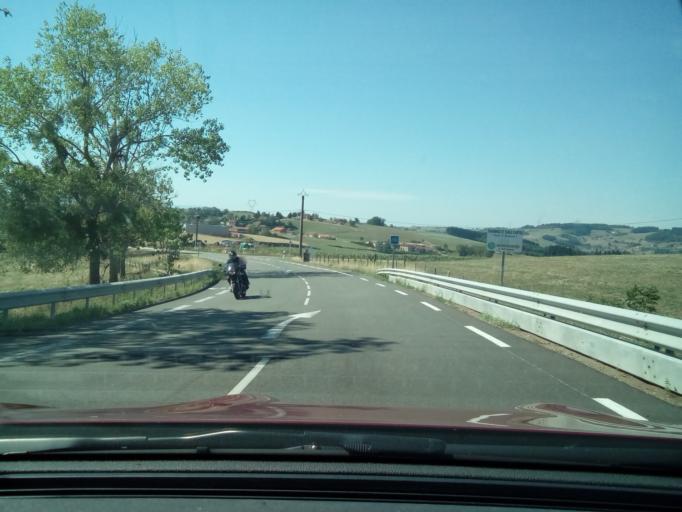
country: FR
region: Rhone-Alpes
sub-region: Departement du Rhone
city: Cublize
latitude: 45.9802
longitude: 4.3824
